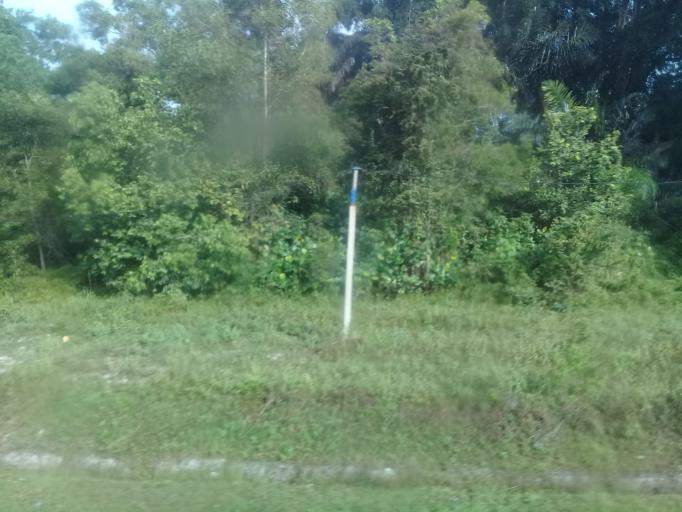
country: MY
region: Perak
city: Batu Gajah
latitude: 4.4767
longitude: 100.9985
